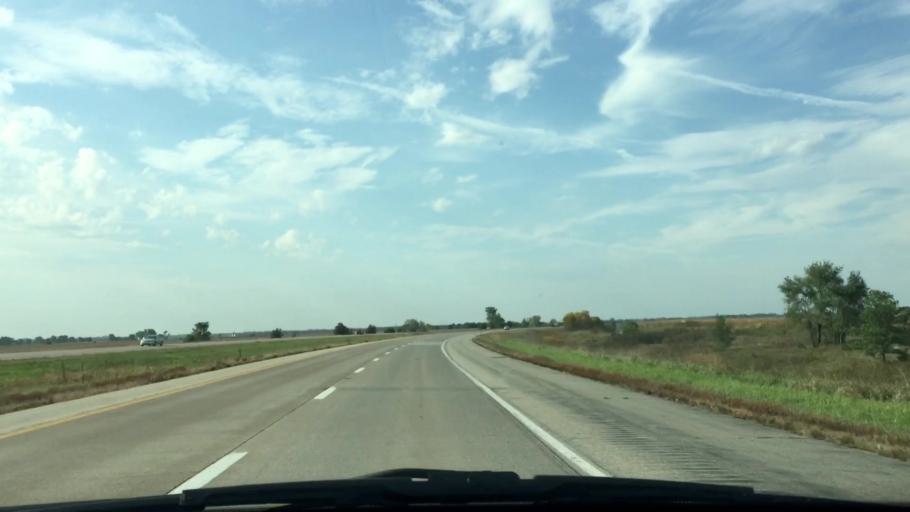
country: US
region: Illinois
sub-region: Whiteside County
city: Erie
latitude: 41.6626
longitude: -90.1443
